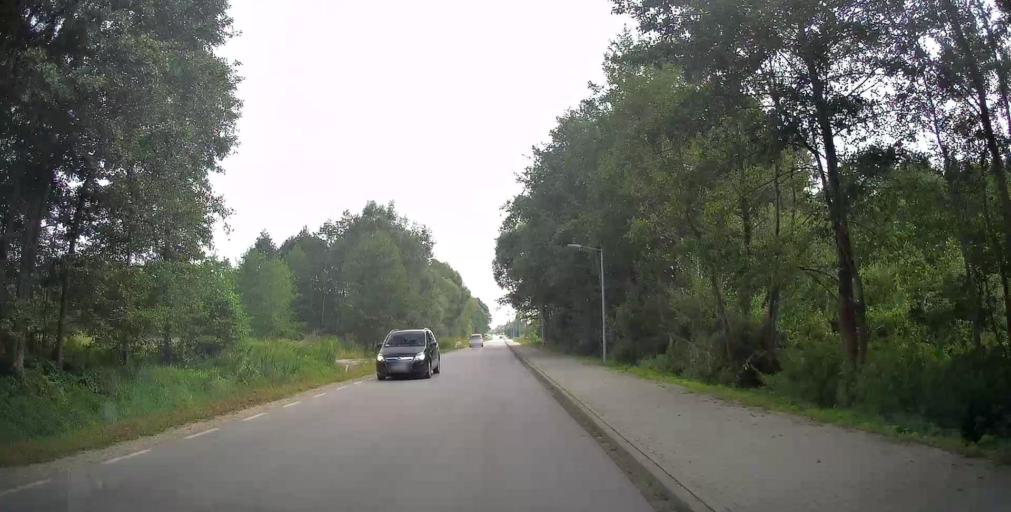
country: PL
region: Masovian Voivodeship
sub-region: Powiat bialobrzeski
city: Sucha
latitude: 51.6140
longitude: 20.9644
